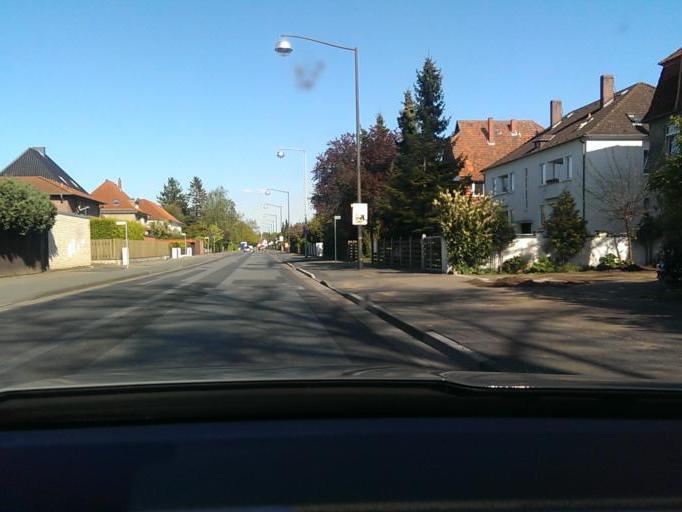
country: DE
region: Lower Saxony
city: Langenhagen
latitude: 52.4527
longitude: 9.7474
